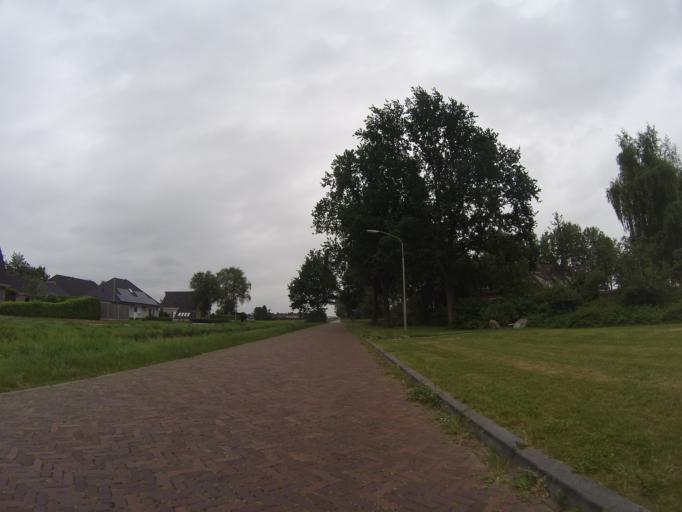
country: NL
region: Drenthe
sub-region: Gemeente Emmen
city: Emmer-Compascuum
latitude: 52.8150
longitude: 7.0579
